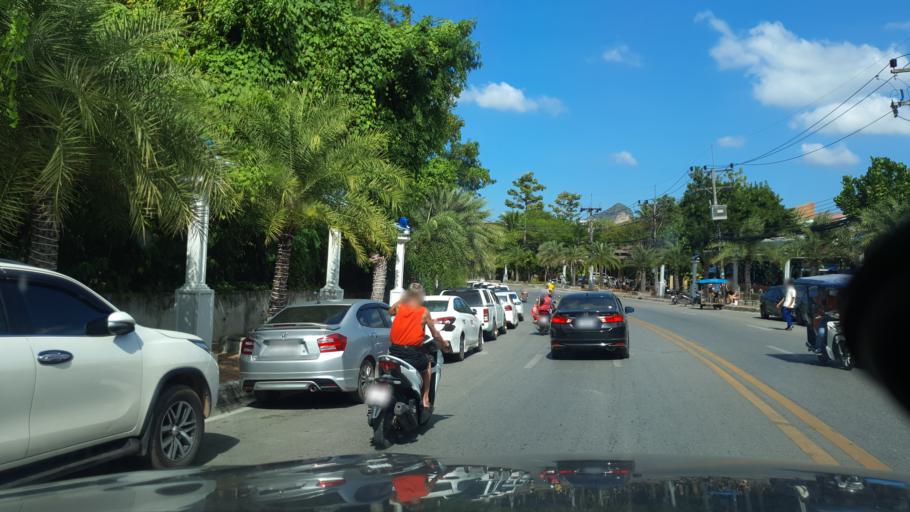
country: TH
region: Phangnga
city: Ban Ao Nang
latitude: 8.0376
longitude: 98.8184
